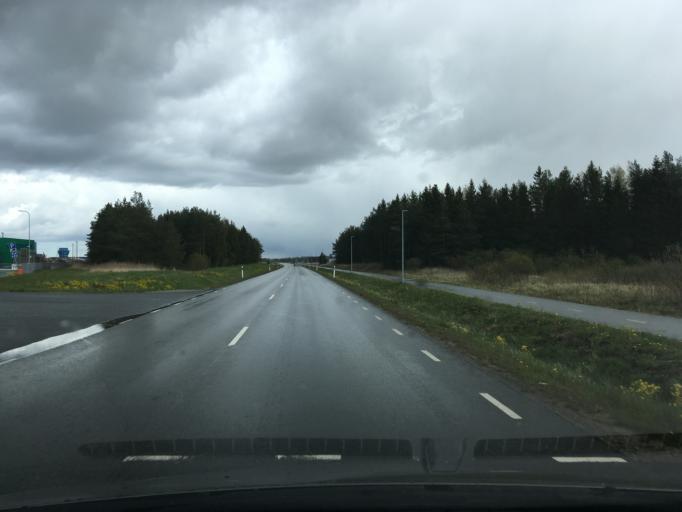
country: EE
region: Harju
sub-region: Joelaehtme vald
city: Loo
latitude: 59.4461
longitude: 24.9439
